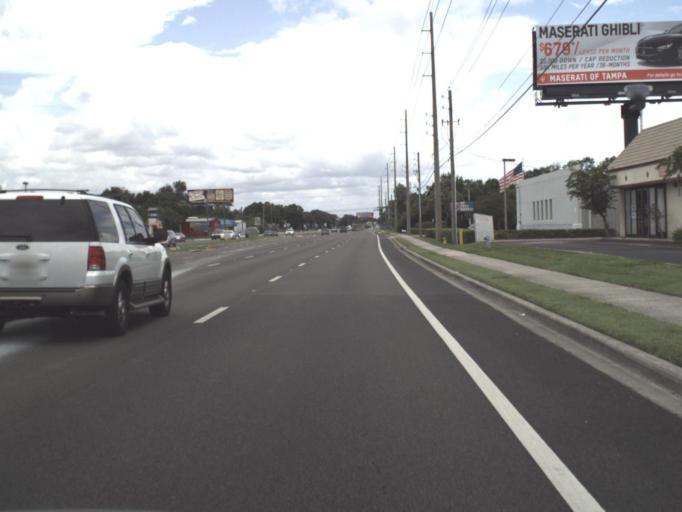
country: US
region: Florida
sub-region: Pinellas County
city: Oldsmar
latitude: 28.0328
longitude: -82.6465
